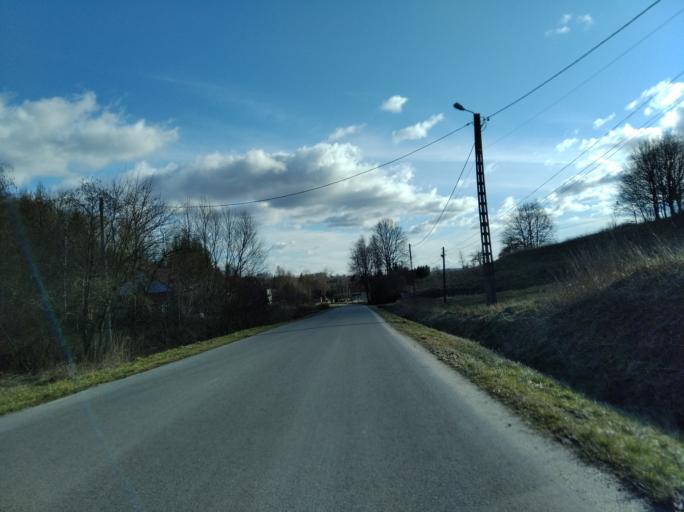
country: PL
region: Subcarpathian Voivodeship
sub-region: Powiat strzyzowski
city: Wisniowa
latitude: 49.8917
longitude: 21.7127
